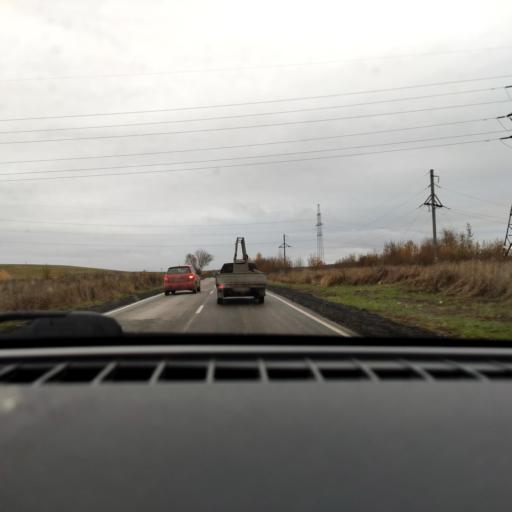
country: RU
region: Perm
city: Ferma
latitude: 57.9201
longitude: 56.3075
